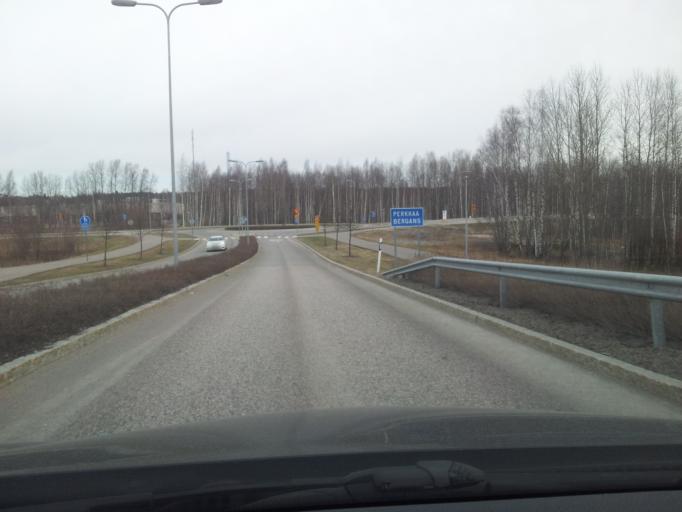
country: FI
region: Uusimaa
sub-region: Helsinki
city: Teekkarikylae
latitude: 60.2105
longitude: 24.8316
